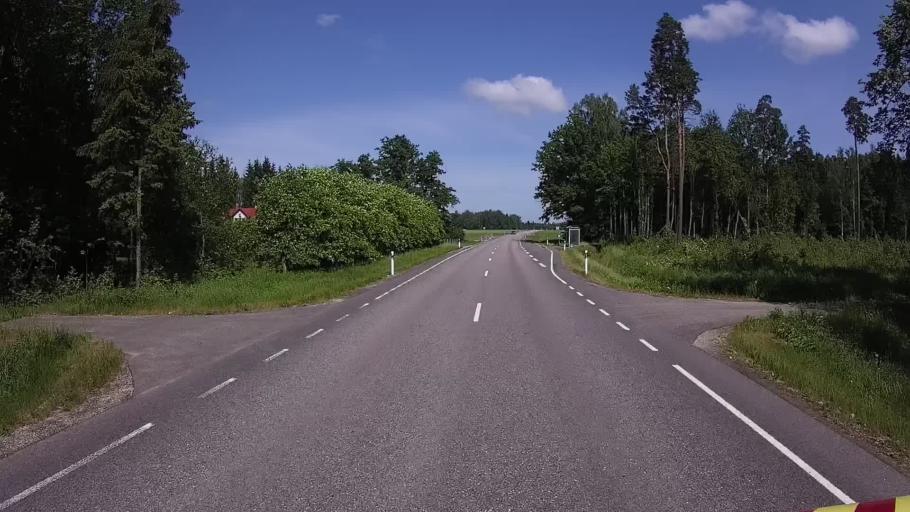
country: EE
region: Tartu
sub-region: Tartu linn
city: Tartu
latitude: 58.3708
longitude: 26.8841
